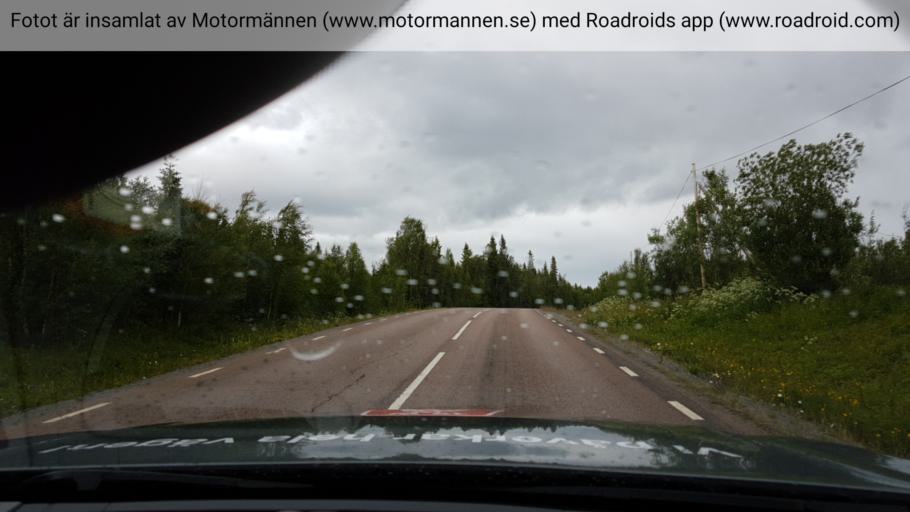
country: SE
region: Jaemtland
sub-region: Krokoms Kommun
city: Valla
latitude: 63.1171
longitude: 13.9133
